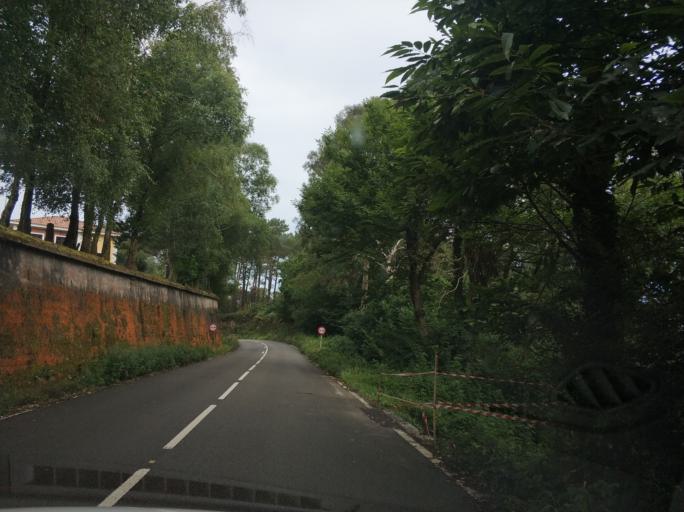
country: ES
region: Asturias
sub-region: Province of Asturias
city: Cudillero
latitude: 43.5576
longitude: -6.2886
